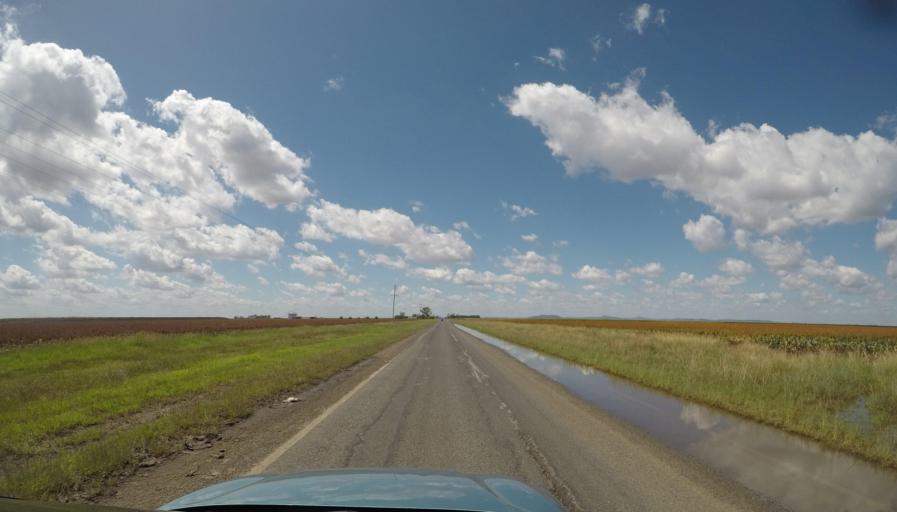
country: AU
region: Queensland
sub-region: Toowoomba
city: Oakey
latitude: -27.5178
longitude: 151.4119
